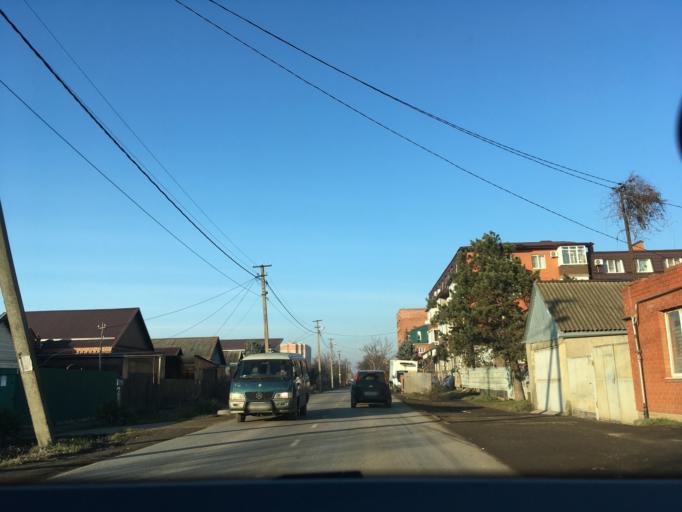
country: RU
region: Krasnodarskiy
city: Krasnodar
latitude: 45.0788
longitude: 39.0207
